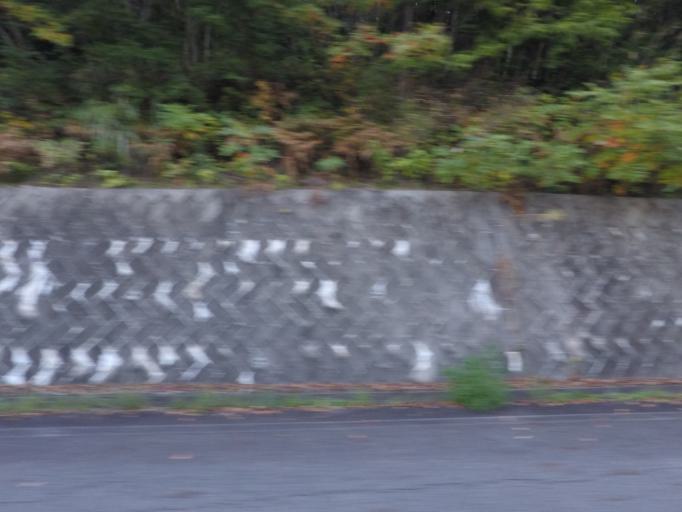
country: JP
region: Nagano
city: Shiojiri
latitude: 35.9889
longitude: 137.7692
